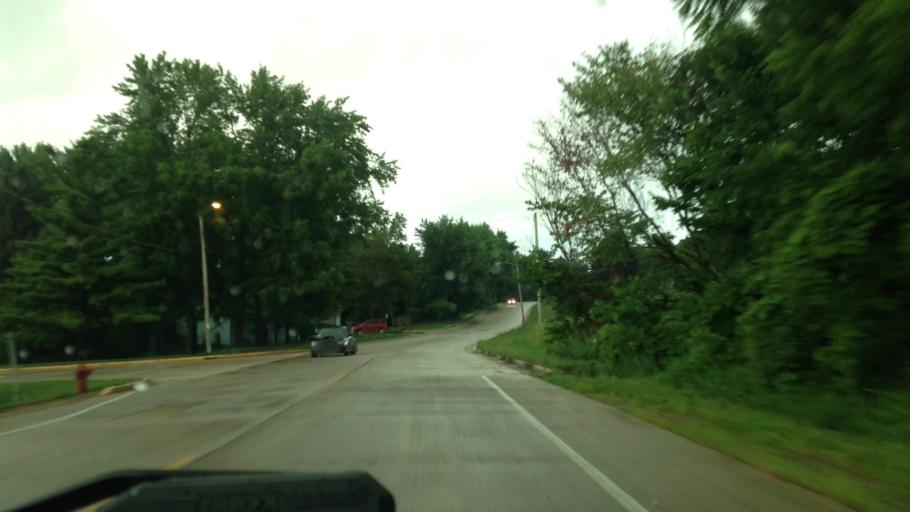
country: US
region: Wisconsin
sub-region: Dodge County
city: Mayville
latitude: 43.4863
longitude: -88.5500
